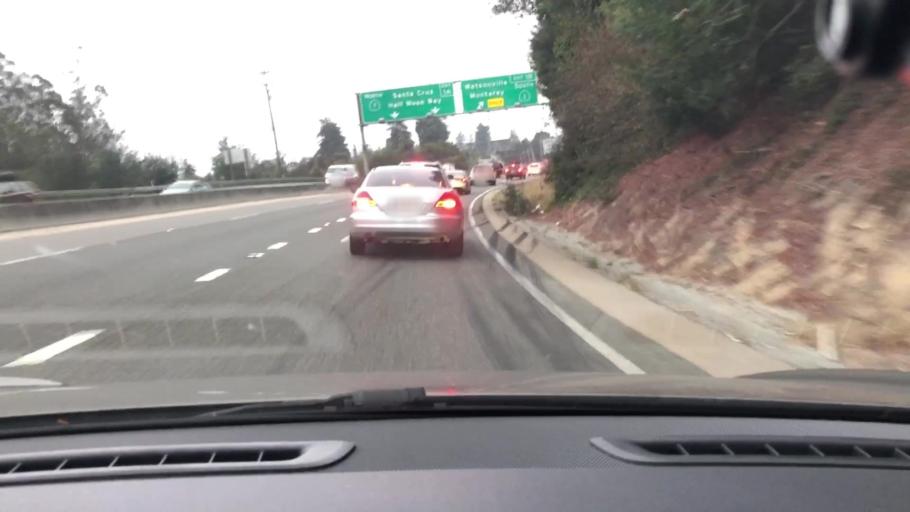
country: US
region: California
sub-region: Santa Cruz County
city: Pasatiempo
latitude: 36.9972
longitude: -122.0209
